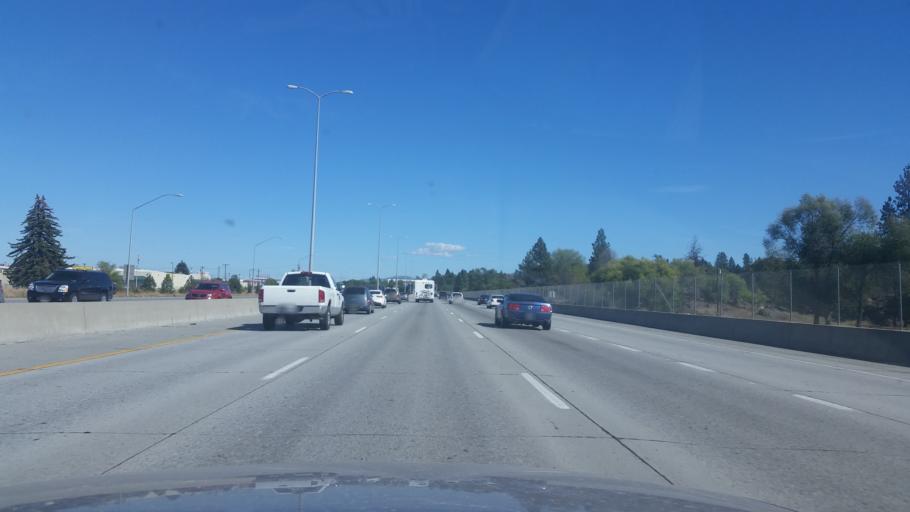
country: US
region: Washington
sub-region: Spokane County
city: Millwood
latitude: 47.6538
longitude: -117.3357
